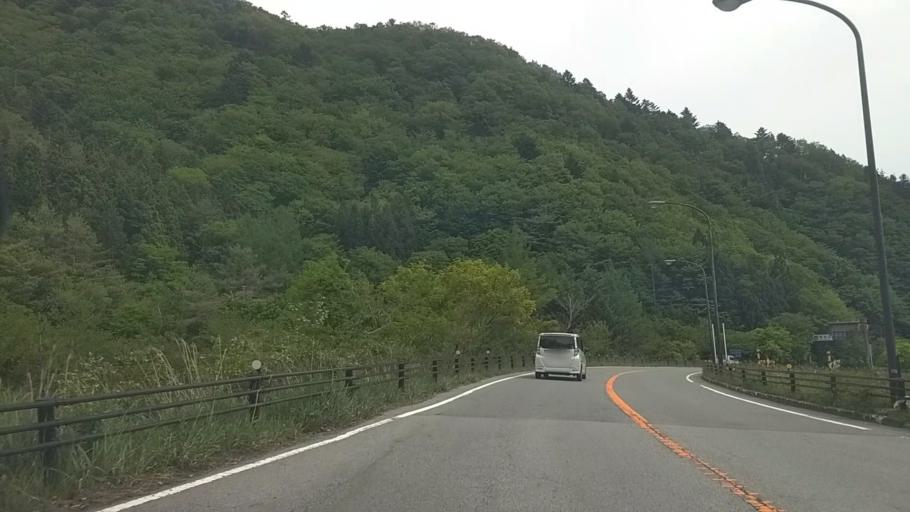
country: JP
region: Yamanashi
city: Fujikawaguchiko
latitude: 35.4951
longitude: 138.6114
